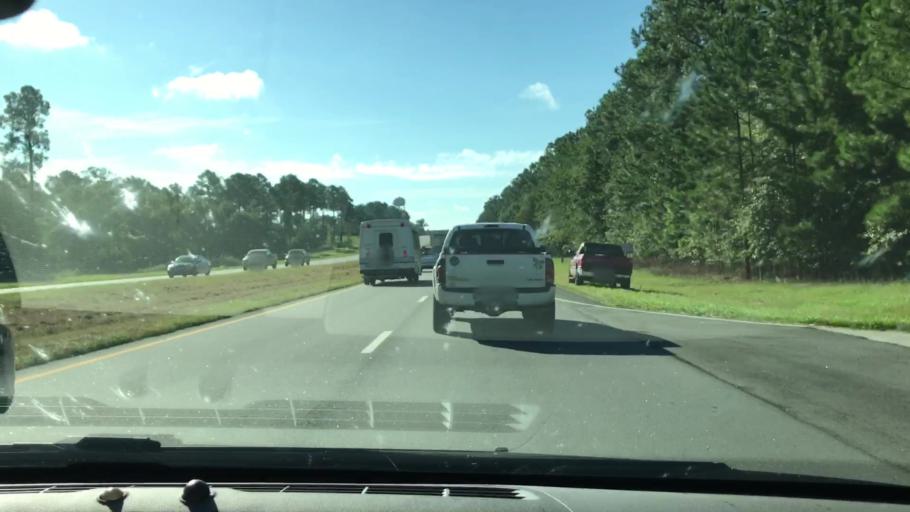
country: US
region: Georgia
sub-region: Dougherty County
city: Albany
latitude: 31.6458
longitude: -84.2585
